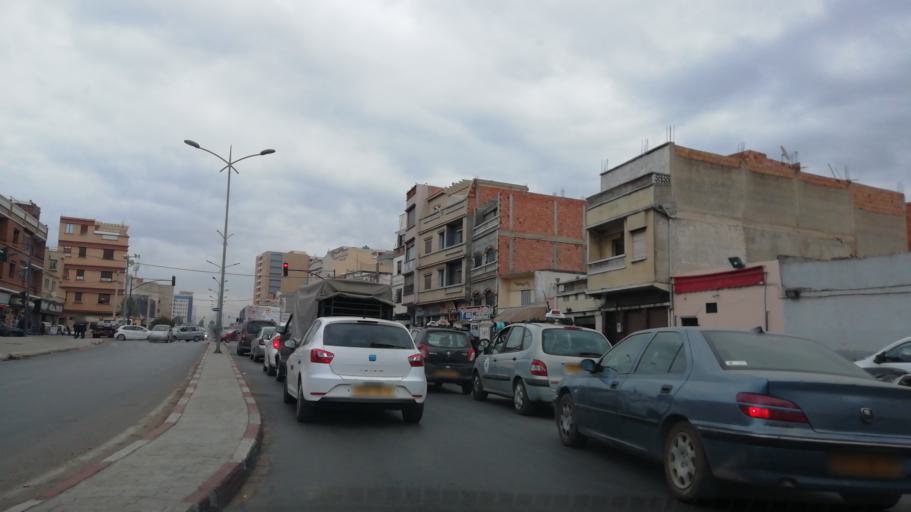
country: DZ
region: Oran
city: Oran
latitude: 35.6867
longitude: -0.6249
